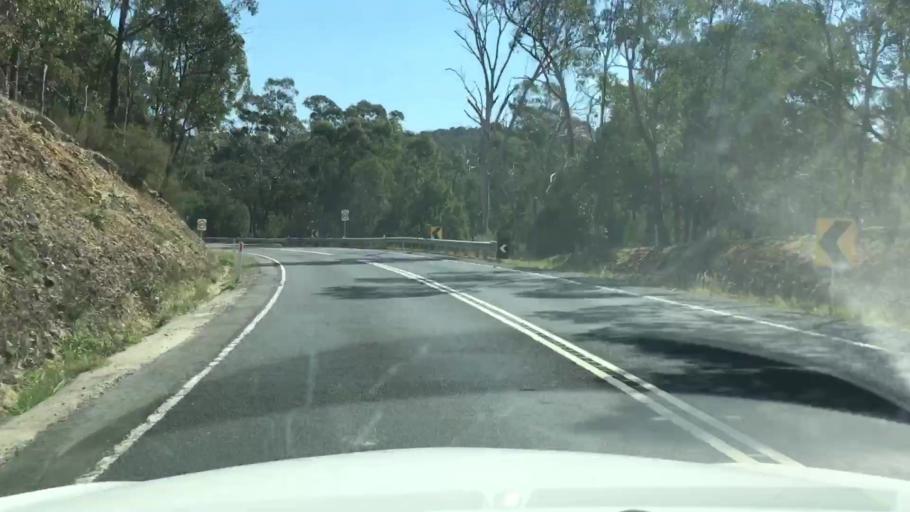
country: AU
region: Victoria
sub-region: Nillumbik
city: Saint Andrews
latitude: -37.6648
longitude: 145.2631
